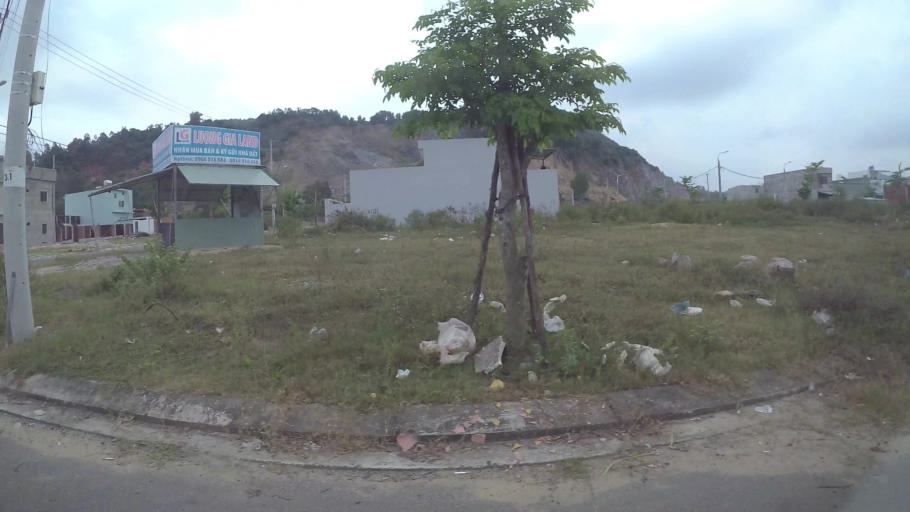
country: VN
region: Da Nang
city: Lien Chieu
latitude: 16.0418
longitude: 108.1685
